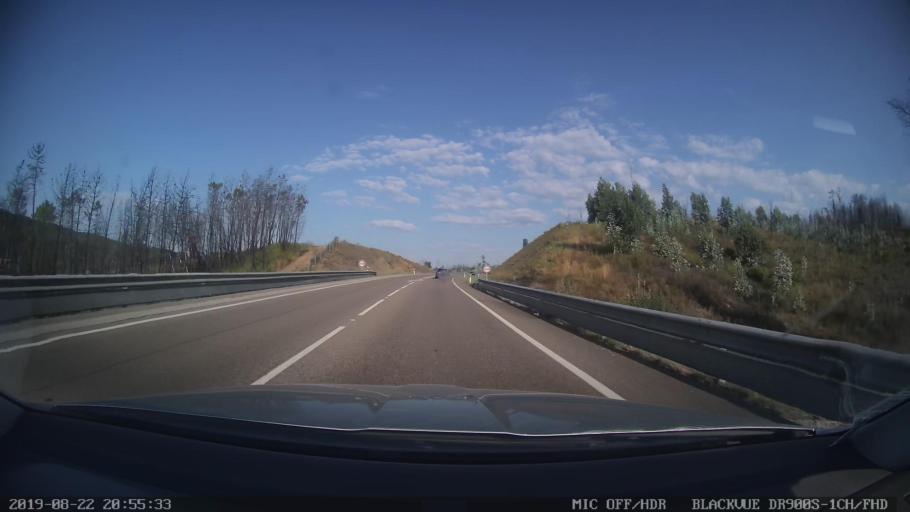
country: PT
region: Castelo Branco
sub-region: Serta
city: Serta
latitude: 39.7810
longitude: -8.0356
